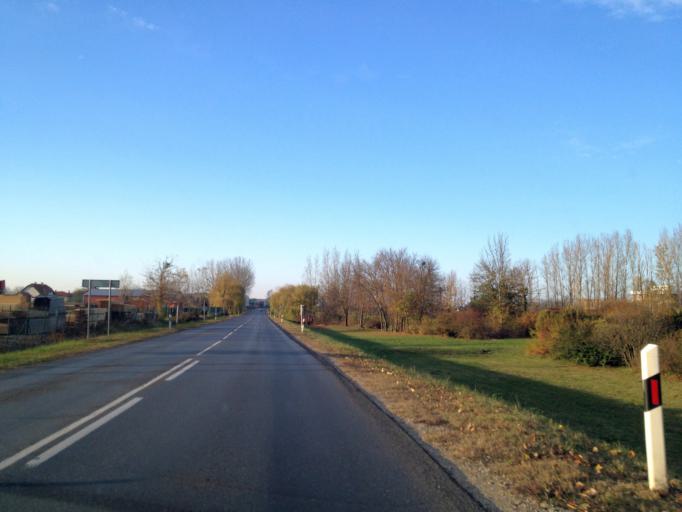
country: HU
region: Gyor-Moson-Sopron
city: Gyorujbarat
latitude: 47.6436
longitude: 17.6626
